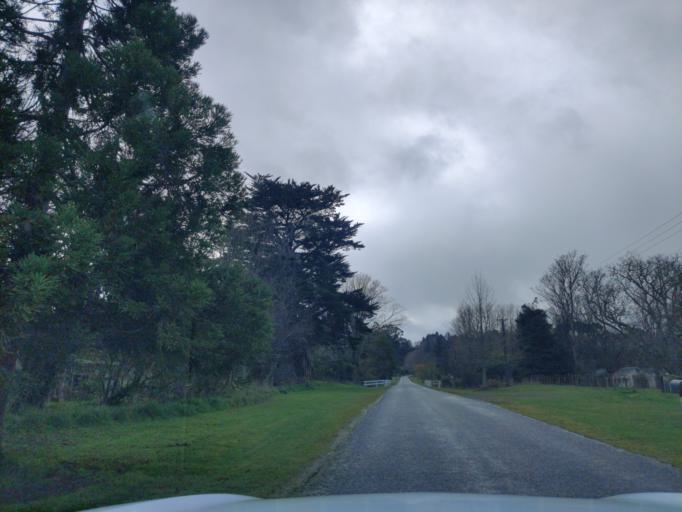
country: NZ
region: Manawatu-Wanganui
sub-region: Palmerston North City
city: Palmerston North
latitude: -40.1712
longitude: 175.7979
